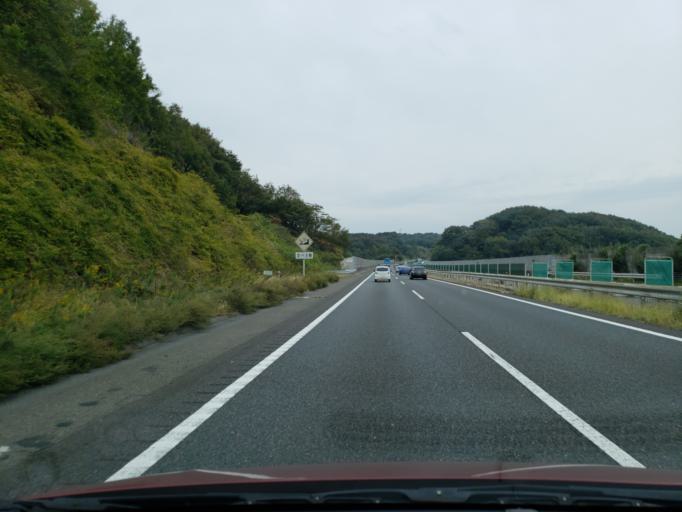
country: JP
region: Hyogo
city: Miki
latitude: 34.8203
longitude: 135.0989
